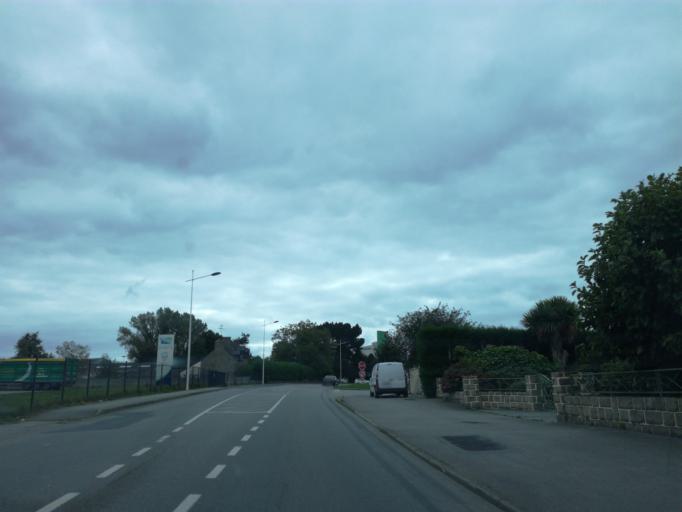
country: FR
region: Brittany
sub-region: Departement des Cotes-d'Armor
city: Loudeac
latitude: 48.1647
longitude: -2.7534
